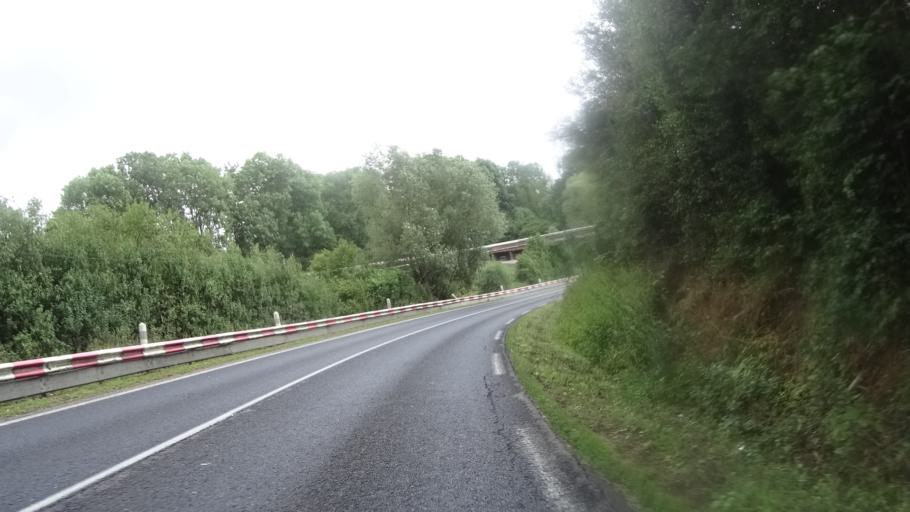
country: FR
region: Lorraine
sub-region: Departement de Meurthe-et-Moselle
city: Art-sur-Meurthe
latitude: 48.6485
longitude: 6.2782
